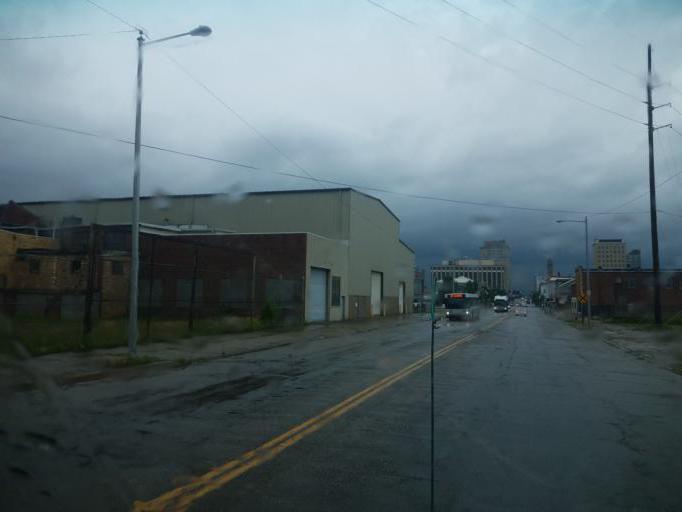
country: US
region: Ohio
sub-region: Stark County
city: Canton
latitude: 40.7973
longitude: -81.3687
